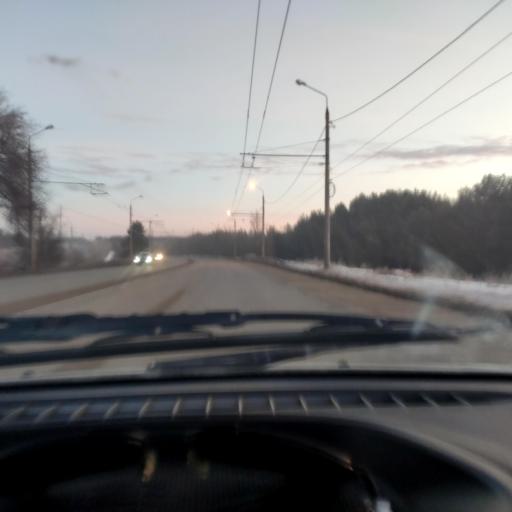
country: RU
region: Samara
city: Zhigulevsk
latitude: 53.4988
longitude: 49.5110
